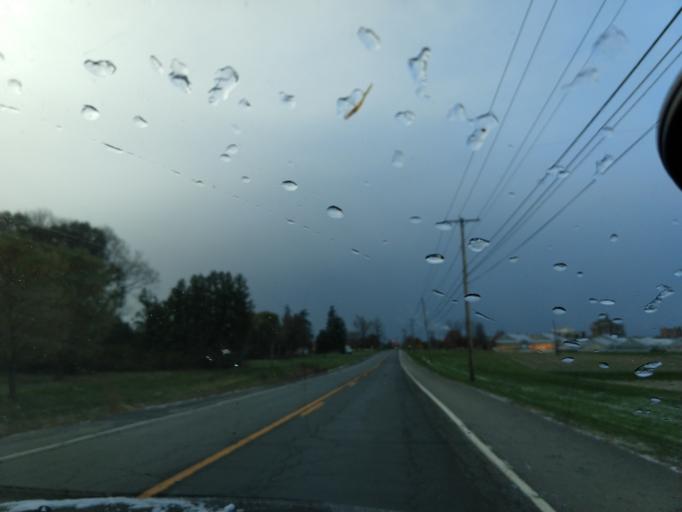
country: US
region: New York
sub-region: Tompkins County
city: Northeast Ithaca
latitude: 42.4481
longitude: -76.4569
